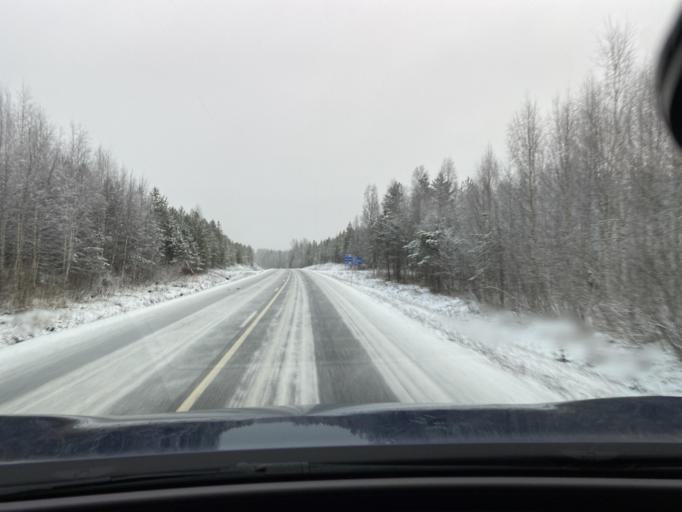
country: FI
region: Northern Ostrobothnia
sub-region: Oulu
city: Yli-Ii
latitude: 65.9309
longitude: 25.8654
